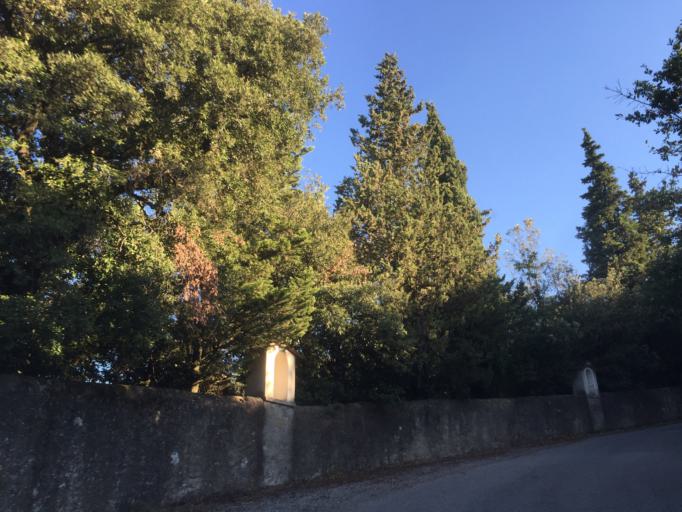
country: IT
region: Tuscany
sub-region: Provincia di Pistoia
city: Pistoia
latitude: 43.9493
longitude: 10.9602
